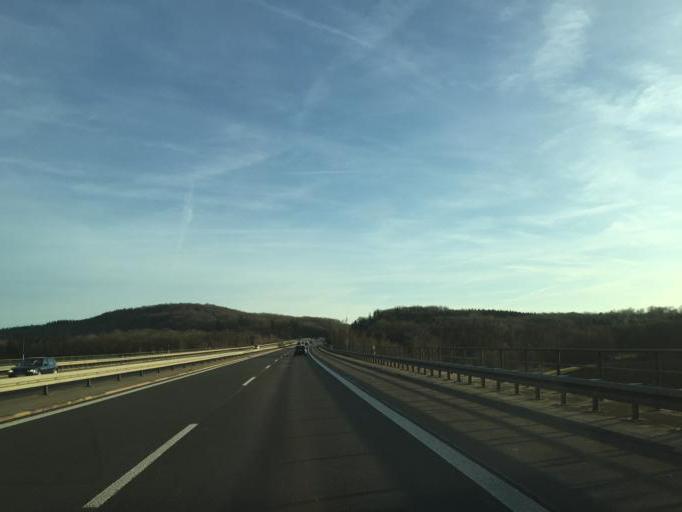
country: DE
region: Bavaria
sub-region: Regierungsbezirk Mittelfranken
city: Gallmersgarten
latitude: 49.4432
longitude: 10.2541
